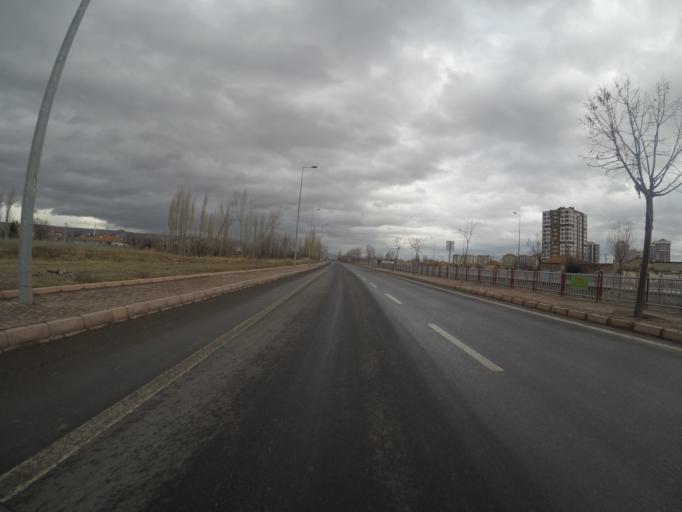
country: TR
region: Kayseri
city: Kayseri
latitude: 38.7514
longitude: 35.4758
